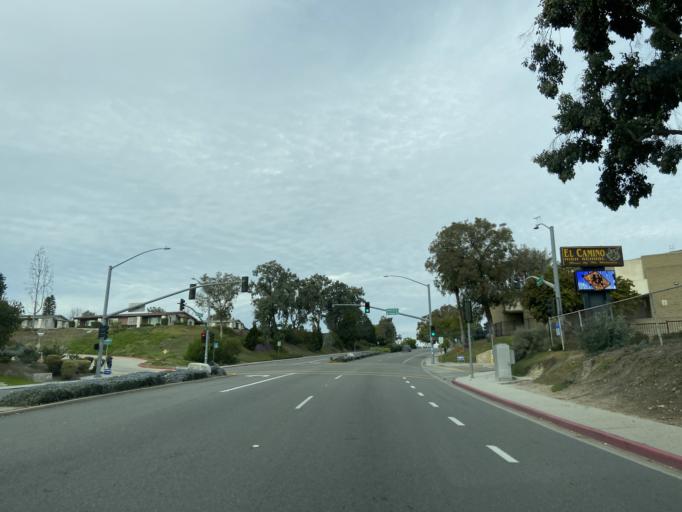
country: US
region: California
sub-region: San Diego County
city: Camp Pendleton South
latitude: 33.2170
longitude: -117.3189
